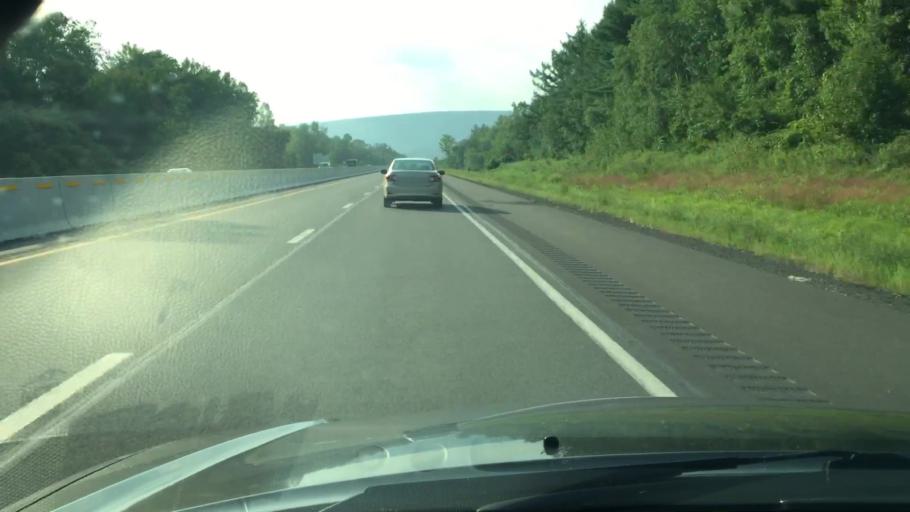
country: US
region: Pennsylvania
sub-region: Luzerne County
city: Nanticoke
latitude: 41.2019
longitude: -75.9712
